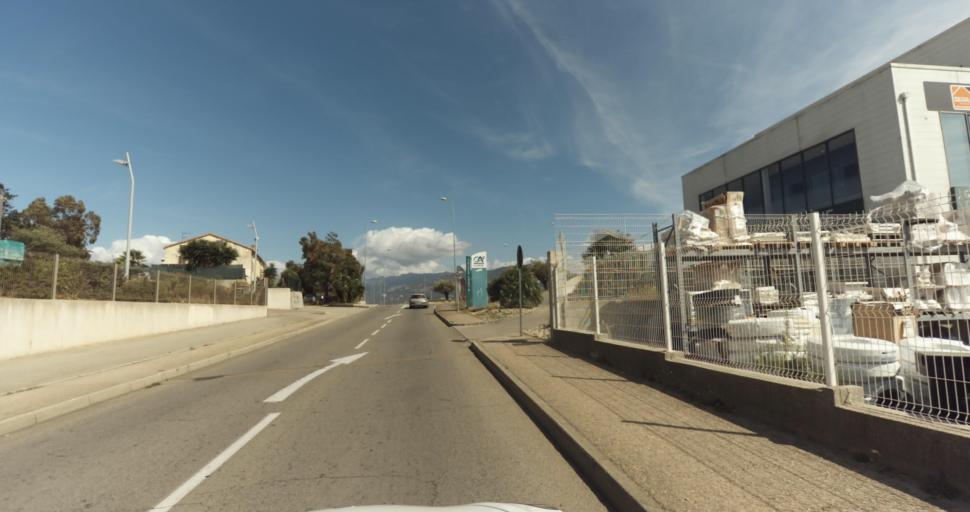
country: FR
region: Corsica
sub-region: Departement de la Corse-du-Sud
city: Alata
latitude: 41.9498
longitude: 8.7704
